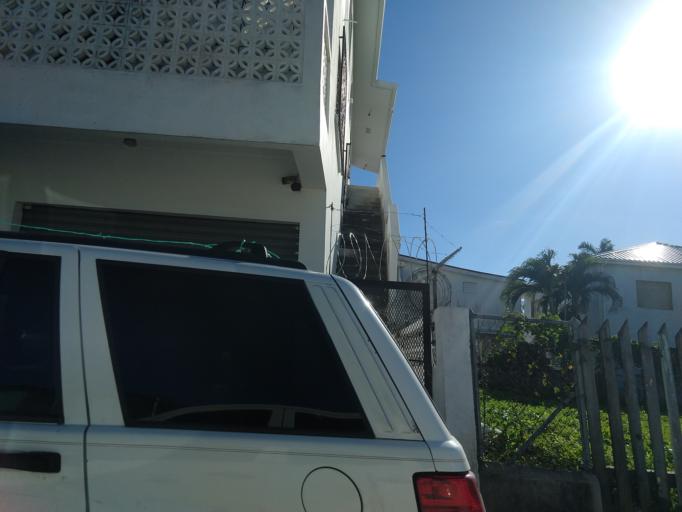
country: BZ
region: Belize
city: Belize City
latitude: 17.5011
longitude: -88.1872
